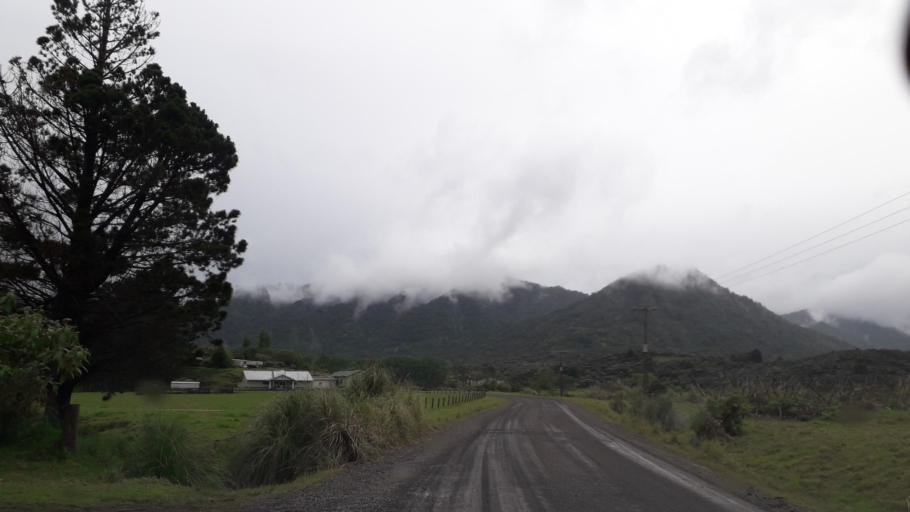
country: NZ
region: Northland
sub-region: Far North District
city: Kaitaia
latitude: -35.4067
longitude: 173.3794
